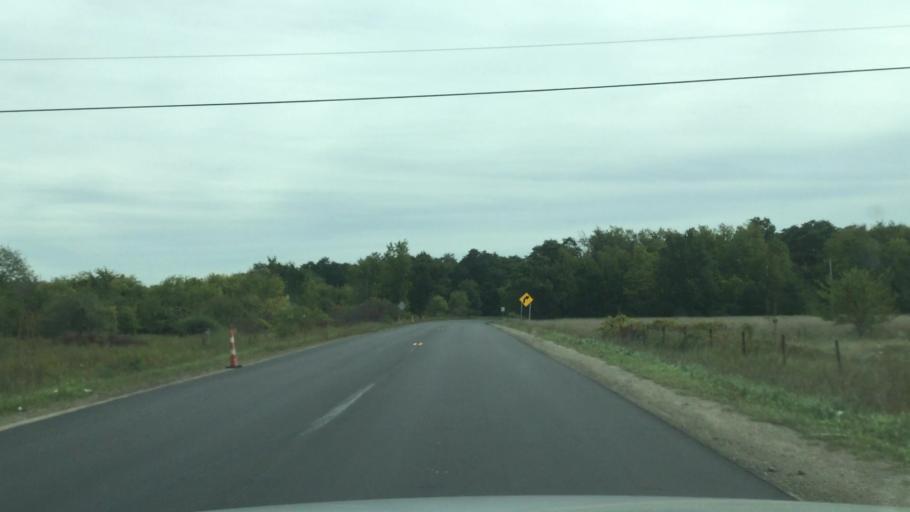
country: US
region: Michigan
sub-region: Oakland County
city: Holly
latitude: 42.8141
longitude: -83.6062
